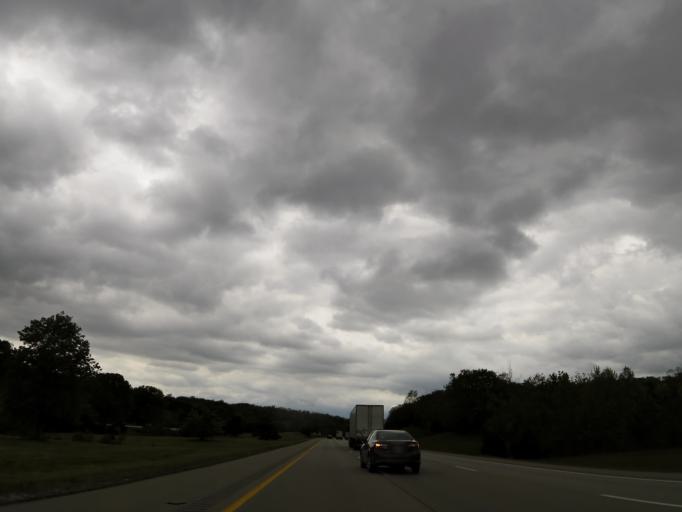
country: US
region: Kentucky
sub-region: Scott County
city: Georgetown
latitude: 38.3385
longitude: -84.5666
